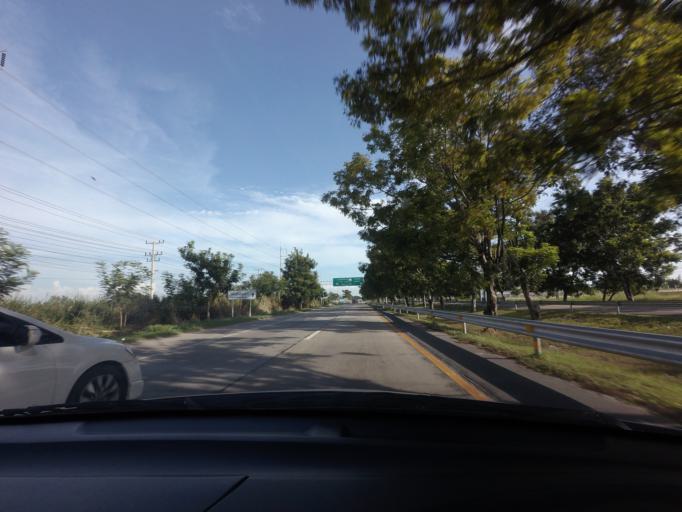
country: TH
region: Phra Nakhon Si Ayutthaya
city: Lat Bua Luang
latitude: 14.1767
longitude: 100.2919
